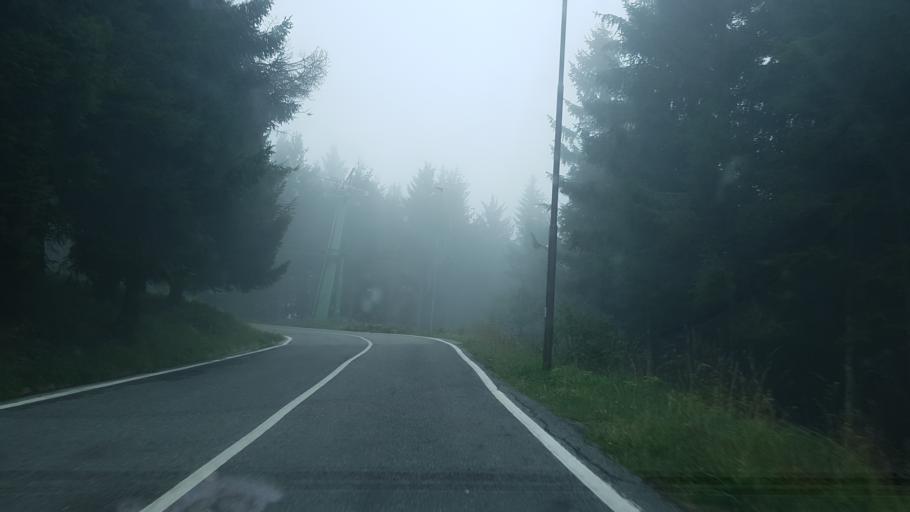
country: IT
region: Piedmont
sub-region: Provincia di Cuneo
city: Frabosa Soprana
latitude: 44.2566
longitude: 7.7929
